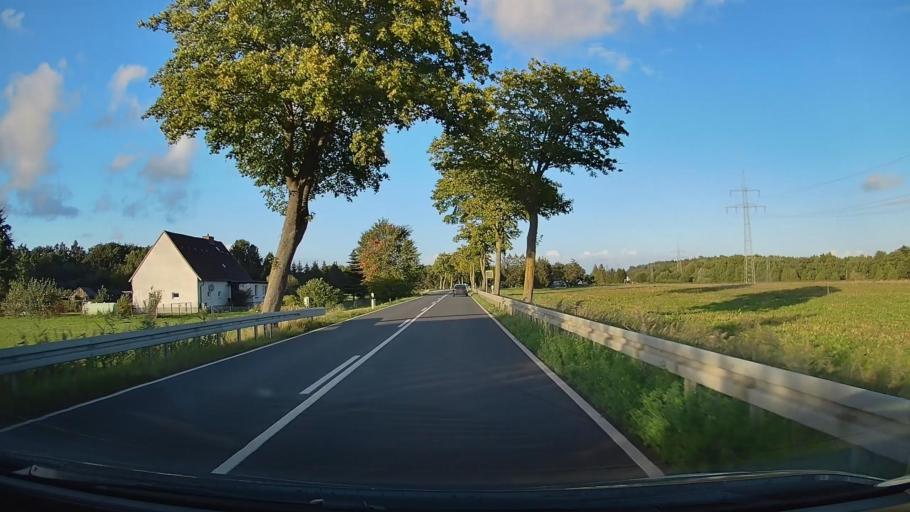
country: DE
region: Mecklenburg-Vorpommern
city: Steinhagen
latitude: 54.2397
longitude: 13.0108
